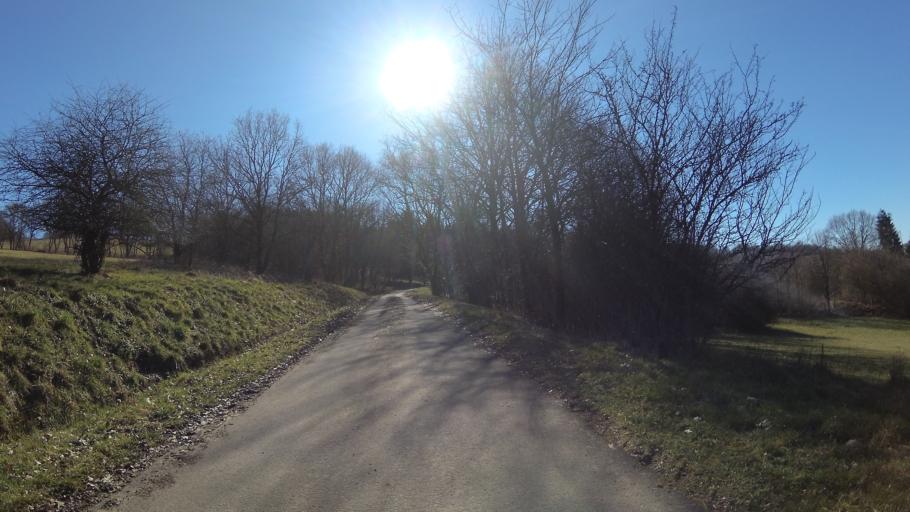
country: DE
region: Rheinland-Pfalz
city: Breitenbach
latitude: 49.4589
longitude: 7.2438
